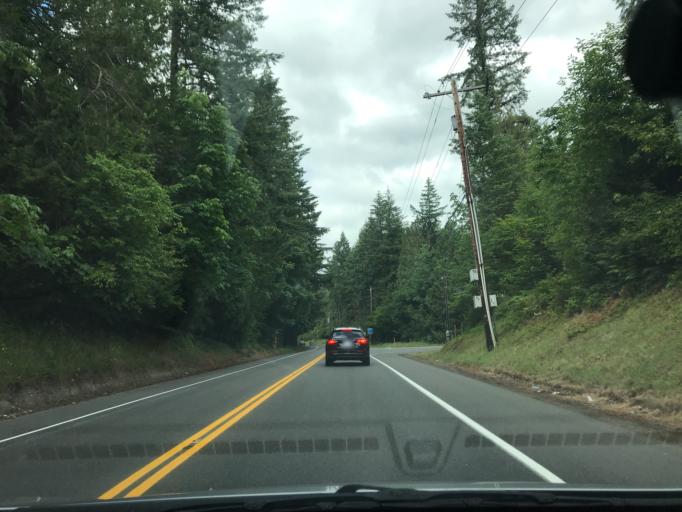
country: US
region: Washington
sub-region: King County
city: Black Diamond
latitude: 47.3008
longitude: -122.0530
